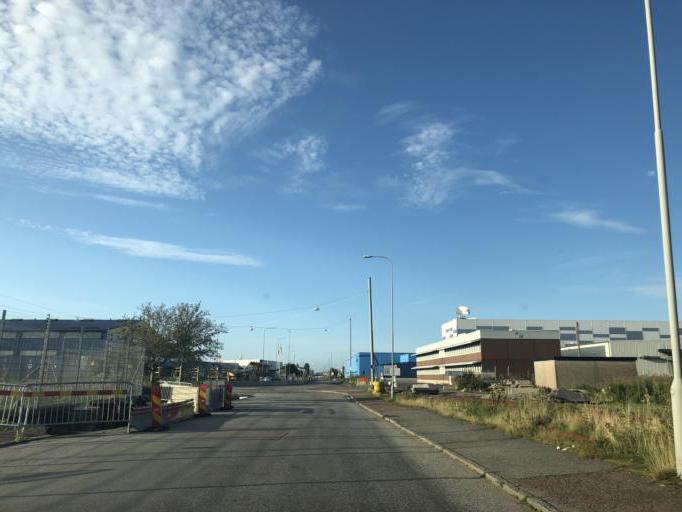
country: SE
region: Vaestra Goetaland
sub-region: Goteborg
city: Goeteborg
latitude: 57.7370
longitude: 11.9929
